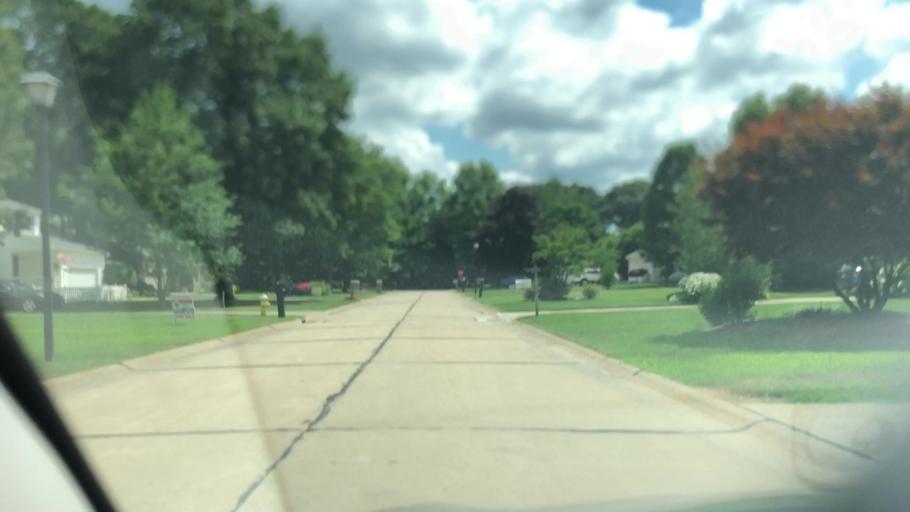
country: US
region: Ohio
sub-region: Summit County
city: Fairlawn
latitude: 41.1230
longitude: -81.6307
